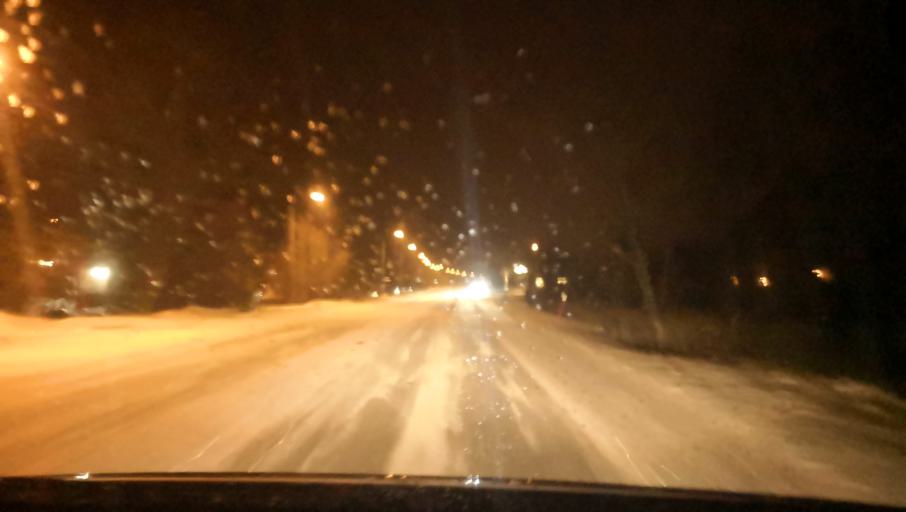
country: SE
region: Uppsala
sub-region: Heby Kommun
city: Tarnsjo
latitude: 60.1611
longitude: 16.9375
